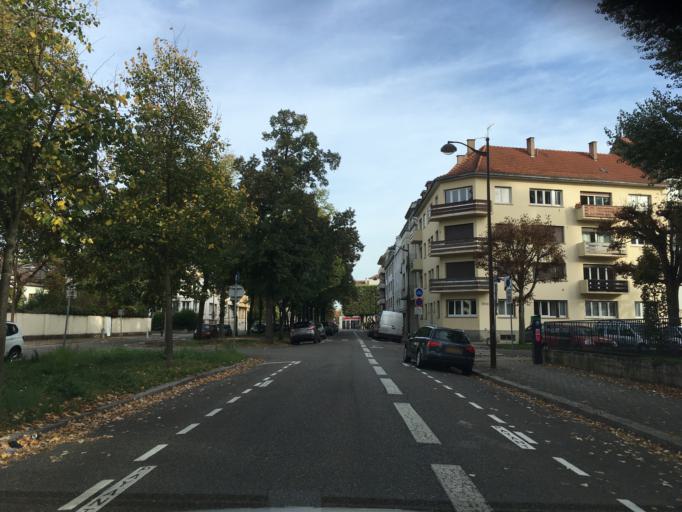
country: FR
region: Alsace
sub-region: Departement du Bas-Rhin
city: Strasbourg
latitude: 48.5876
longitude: 7.7746
